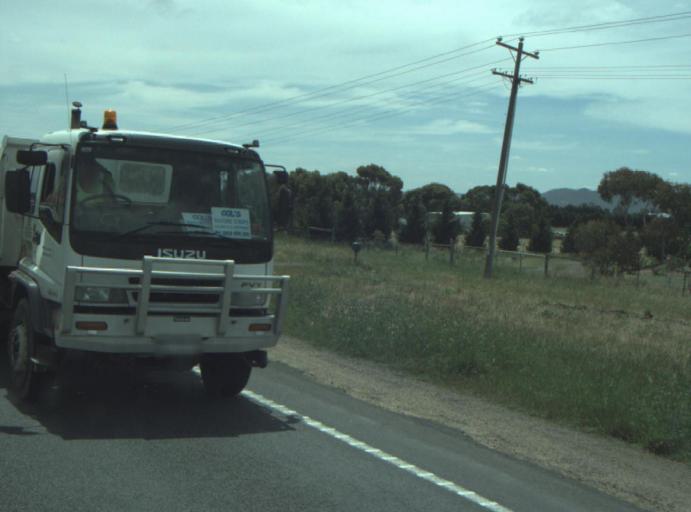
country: AU
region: Victoria
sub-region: Greater Geelong
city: Lara
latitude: -38.0253
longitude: 144.3536
